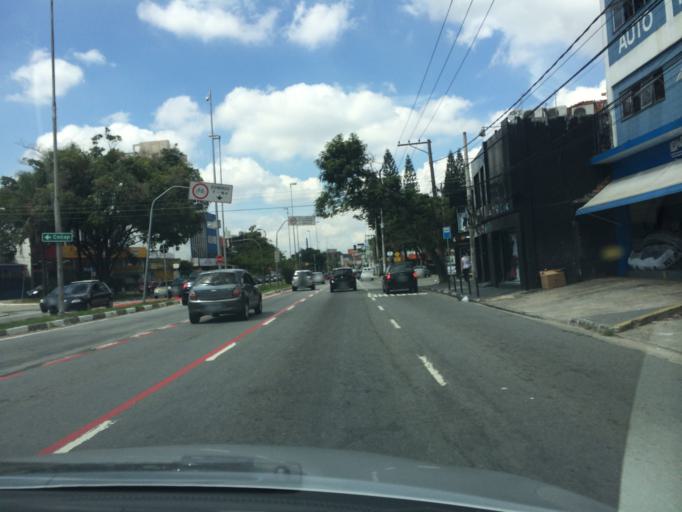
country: BR
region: Sao Paulo
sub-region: Guarulhos
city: Guarulhos
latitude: -23.4658
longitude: -46.5254
